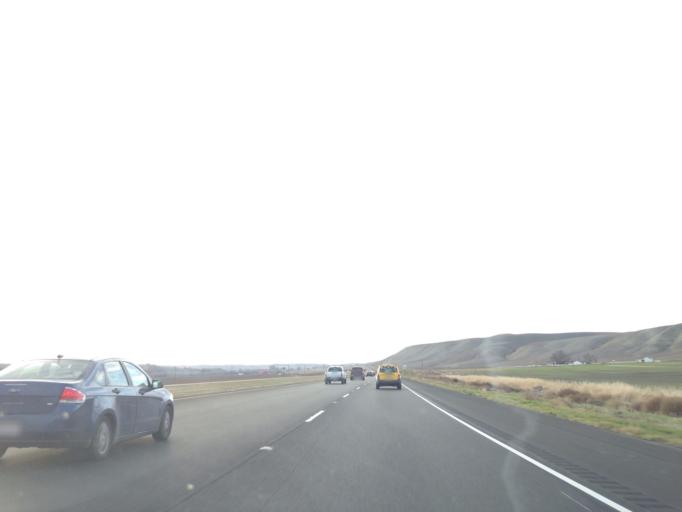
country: US
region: California
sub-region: San Luis Obispo County
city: Shandon
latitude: 35.6617
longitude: -120.4220
